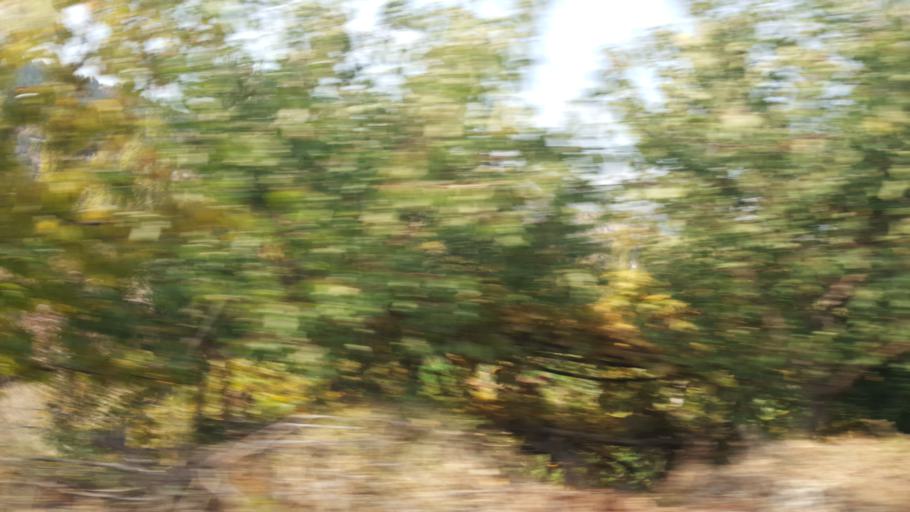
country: TR
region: Eskisehir
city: Mihaliccik
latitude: 39.9791
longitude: 31.3714
